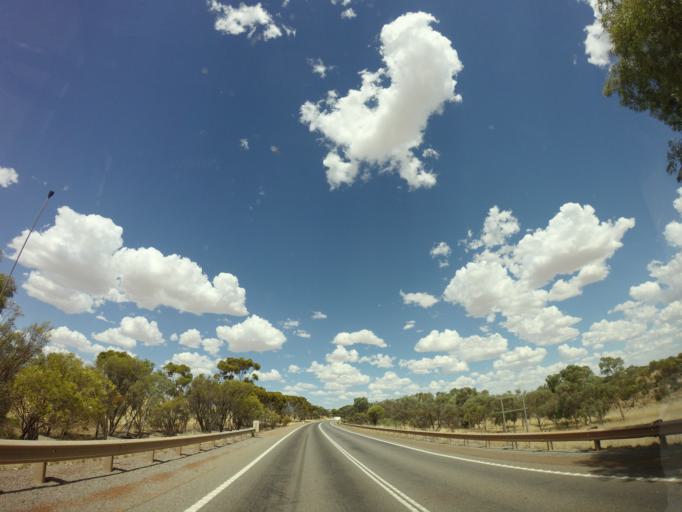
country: AU
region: Western Australia
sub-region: Northam
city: Northam
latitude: -31.6337
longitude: 116.7982
